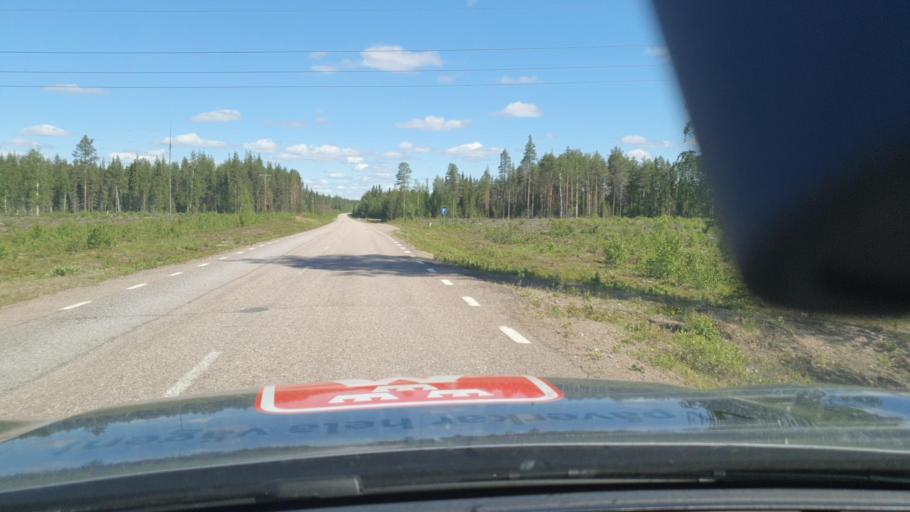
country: SE
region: Norrbotten
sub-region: Overkalix Kommun
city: OEverkalix
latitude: 67.0603
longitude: 22.5130
